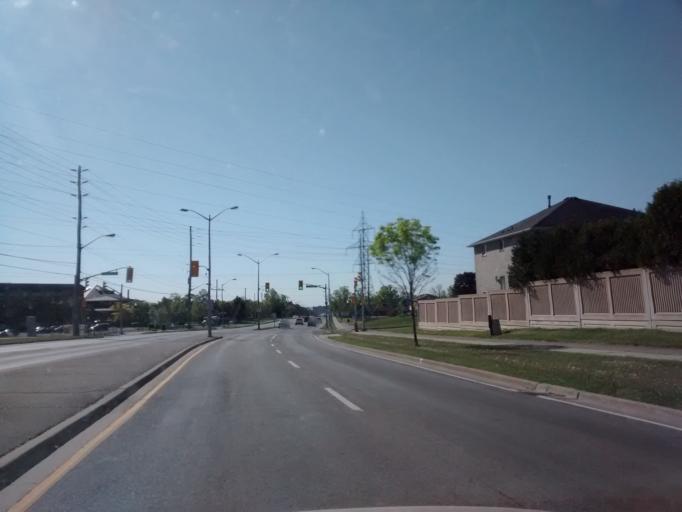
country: CA
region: Ontario
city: Burlington
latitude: 43.3634
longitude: -79.8199
